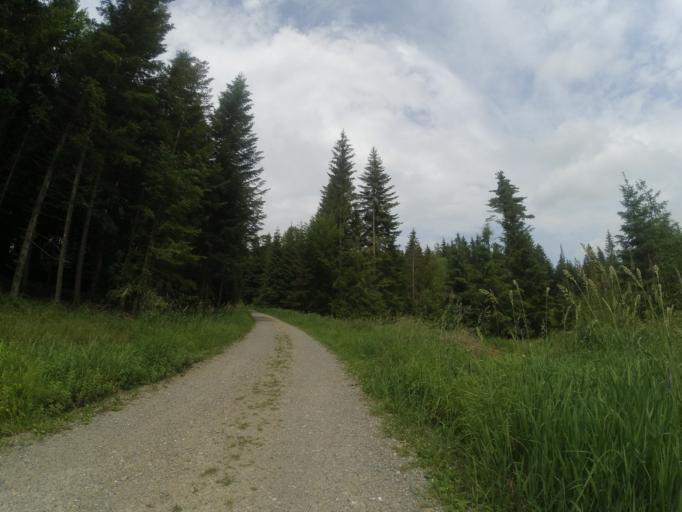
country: DE
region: Baden-Wuerttemberg
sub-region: Tuebingen Region
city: Leutkirch im Allgau
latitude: 47.7669
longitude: 10.0033
